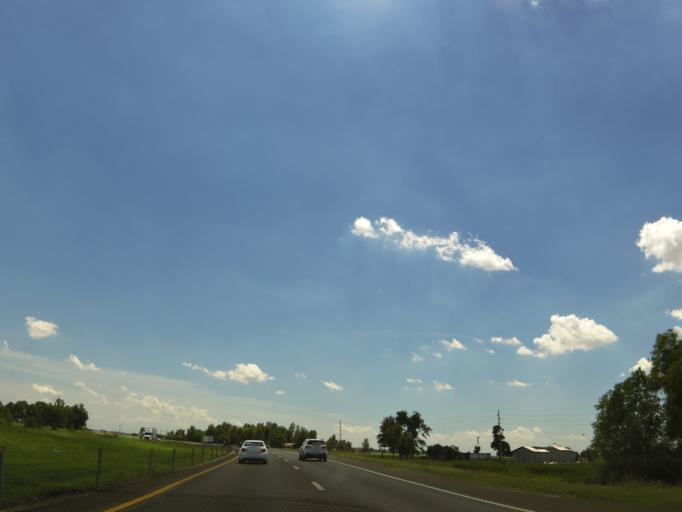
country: US
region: Missouri
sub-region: New Madrid County
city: Portageville
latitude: 36.3873
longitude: -89.7010
